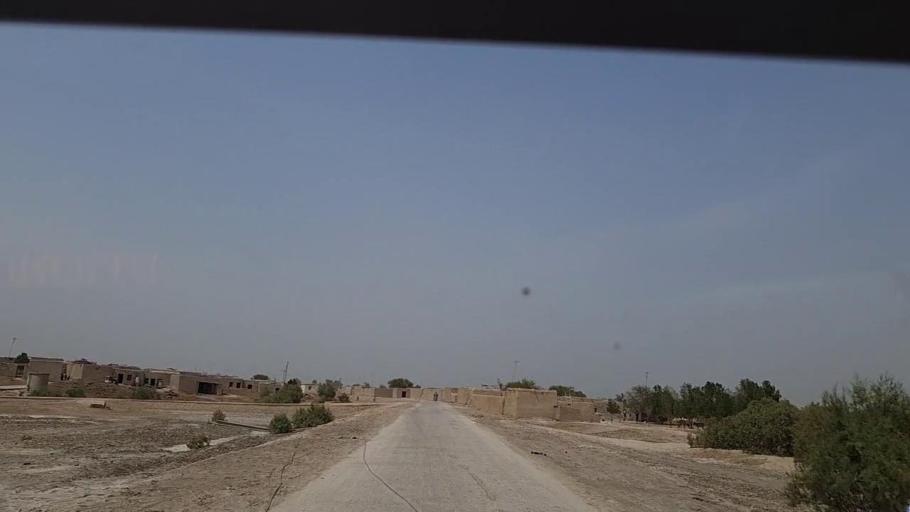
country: PK
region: Sindh
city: Khairpur Nathan Shah
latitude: 27.0665
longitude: 67.6498
